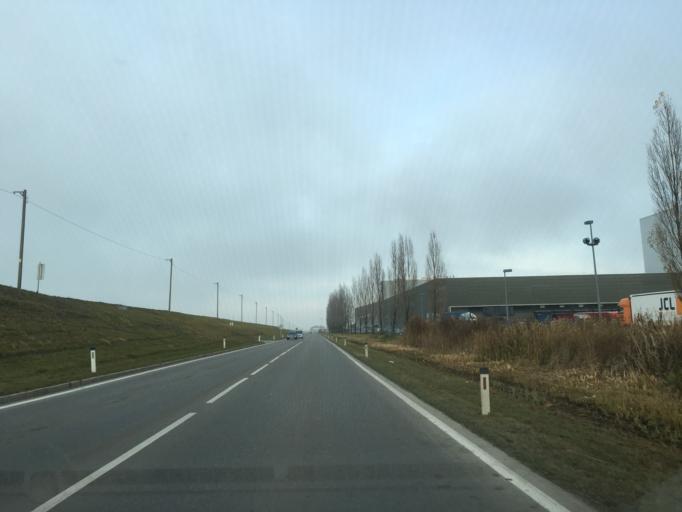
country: AT
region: Vorarlberg
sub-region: Politischer Bezirk Bregenz
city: Fussach
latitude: 47.4658
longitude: 9.6708
